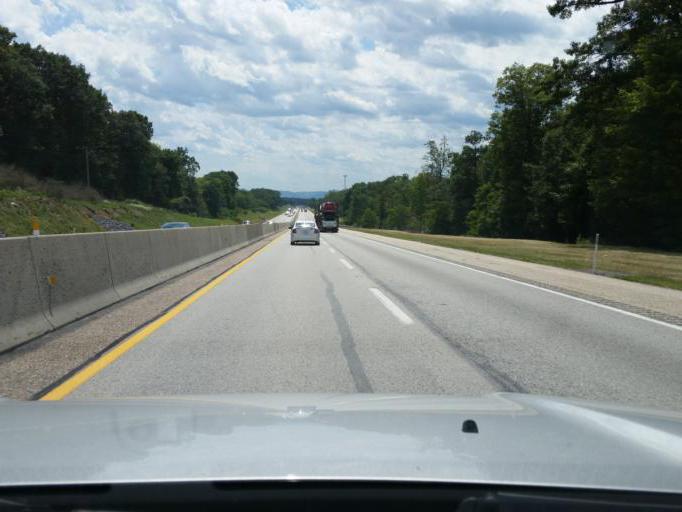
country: US
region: Pennsylvania
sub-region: Franklin County
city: Doylestown
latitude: 40.1504
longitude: -77.7163
